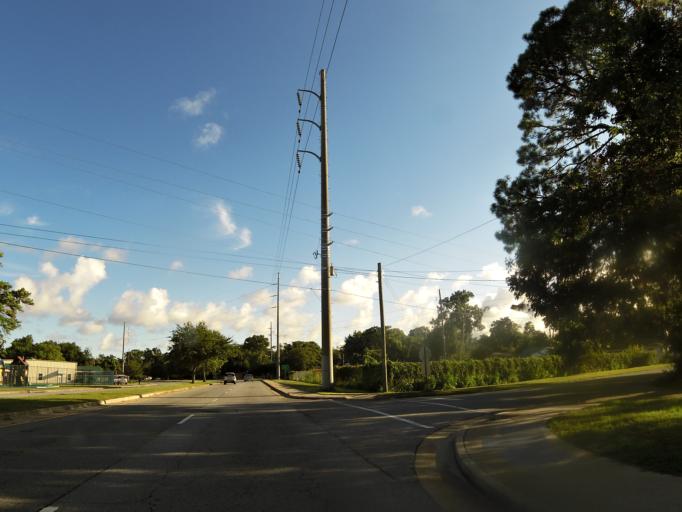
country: US
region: Georgia
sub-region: Glynn County
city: Brunswick
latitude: 31.1673
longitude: -81.4930
